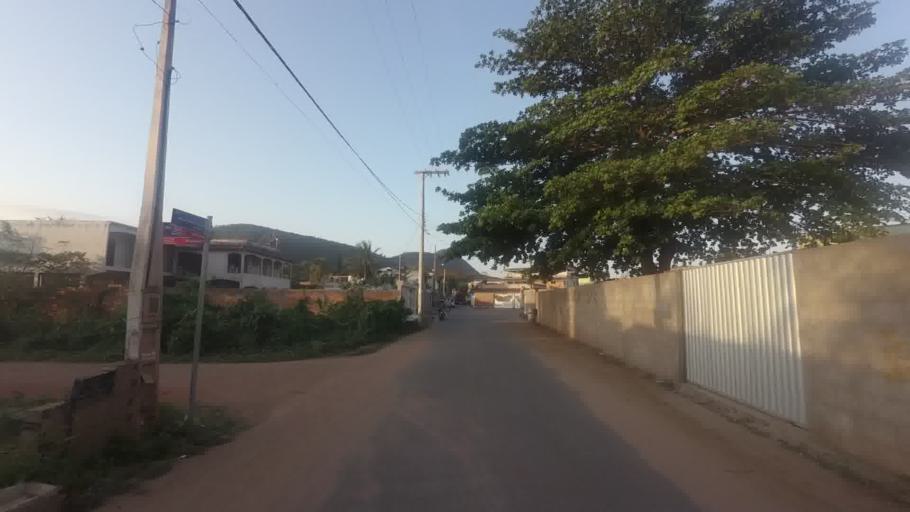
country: BR
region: Espirito Santo
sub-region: Piuma
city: Piuma
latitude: -20.8891
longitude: -40.7810
